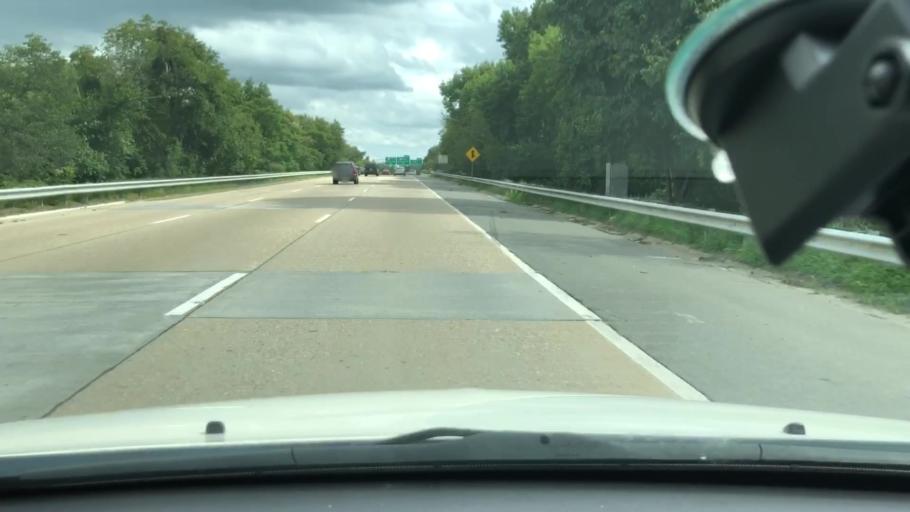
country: US
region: Virginia
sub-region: City of Chesapeake
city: Chesapeake
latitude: 36.7650
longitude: -76.2697
